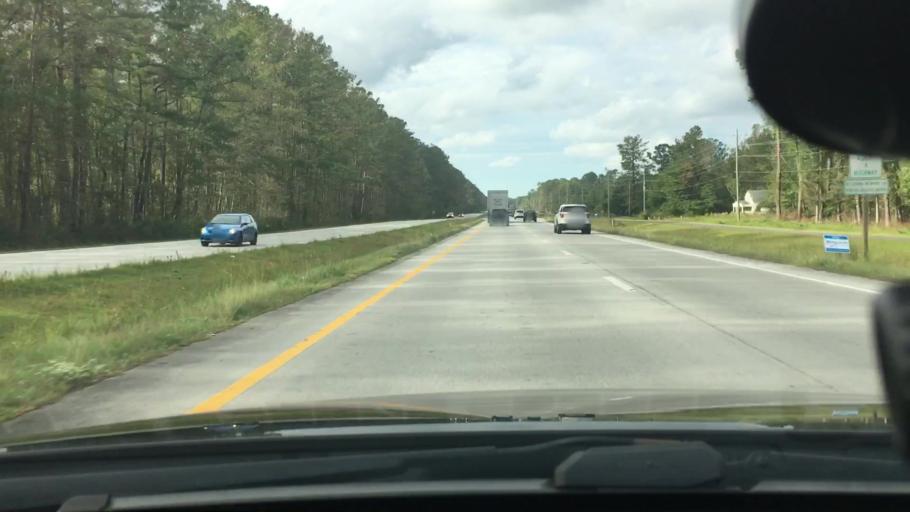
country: US
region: North Carolina
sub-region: Craven County
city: Neuse Forest
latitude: 34.9749
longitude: -76.9743
